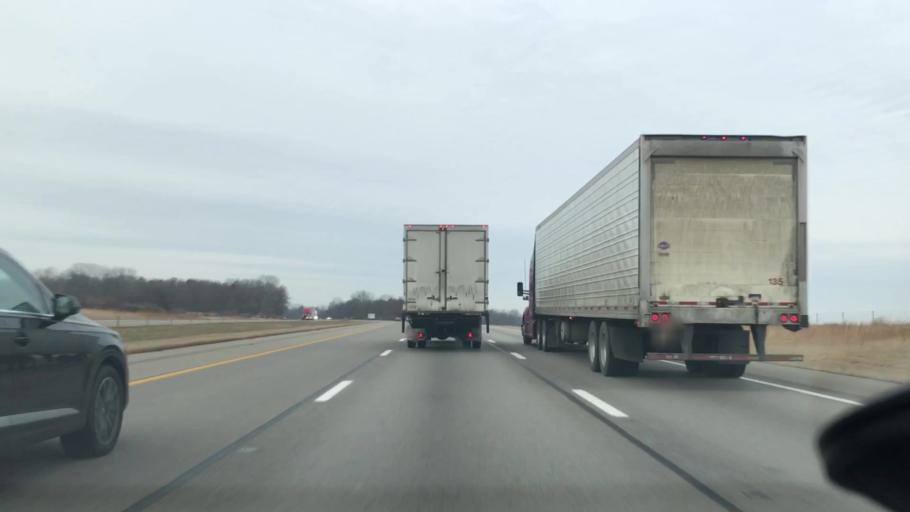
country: US
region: Ohio
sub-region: Clark County
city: Lisbon
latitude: 39.9347
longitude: -83.6670
